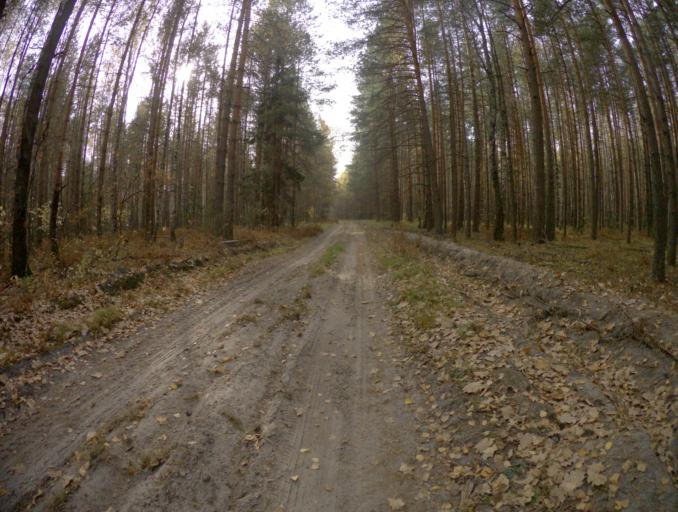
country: RU
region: Vladimir
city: Vorsha
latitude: 55.9542
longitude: 40.1414
